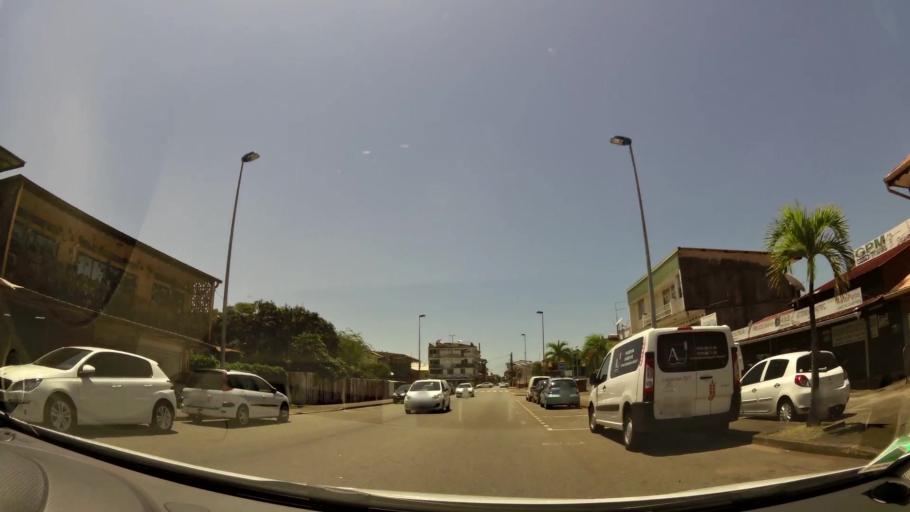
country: GF
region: Guyane
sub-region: Guyane
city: Cayenne
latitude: 4.9358
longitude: -52.3275
